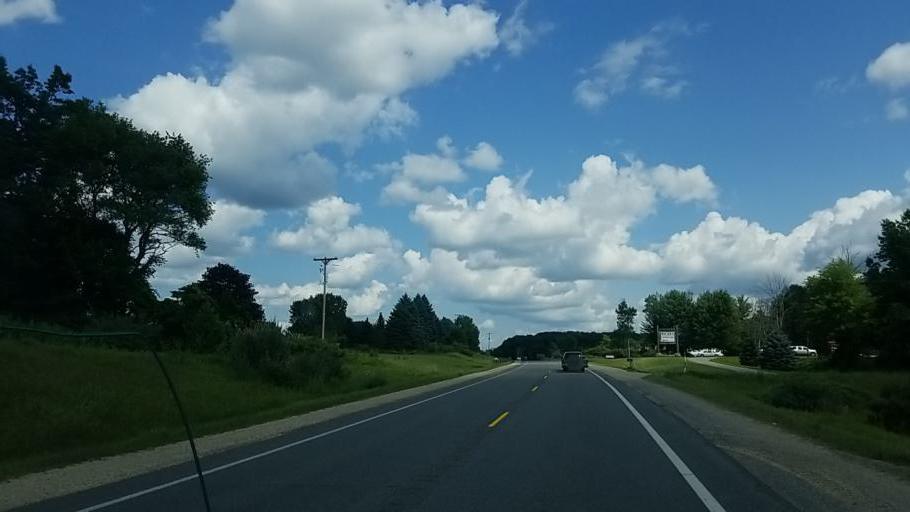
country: US
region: Michigan
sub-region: Newaygo County
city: Newaygo
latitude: 43.3960
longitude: -85.6478
